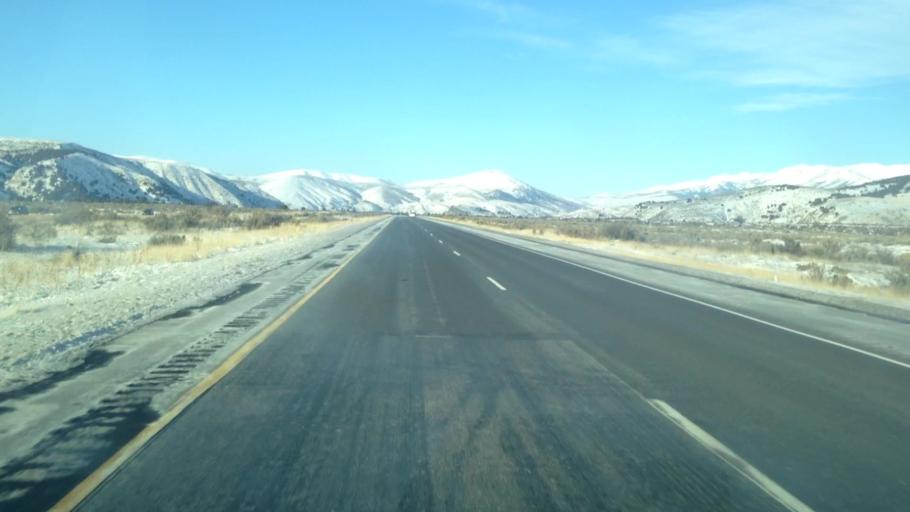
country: US
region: Idaho
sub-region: Bannock County
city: Pocatello
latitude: 42.7484
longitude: -112.2262
